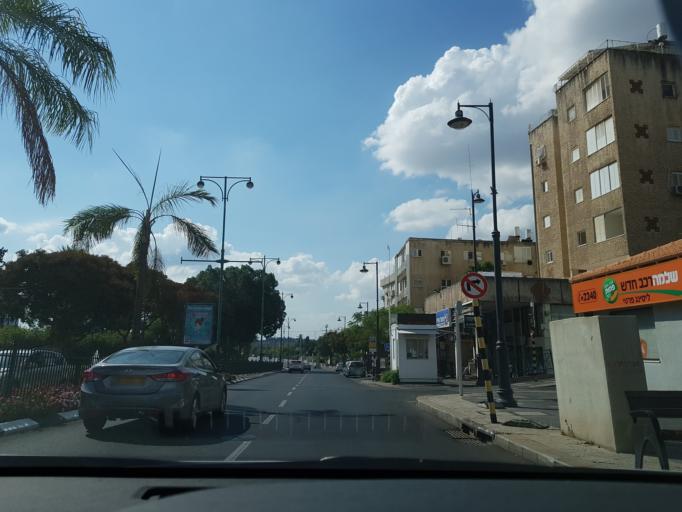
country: IL
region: Central District
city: Ness Ziona
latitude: 31.9268
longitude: 34.7979
